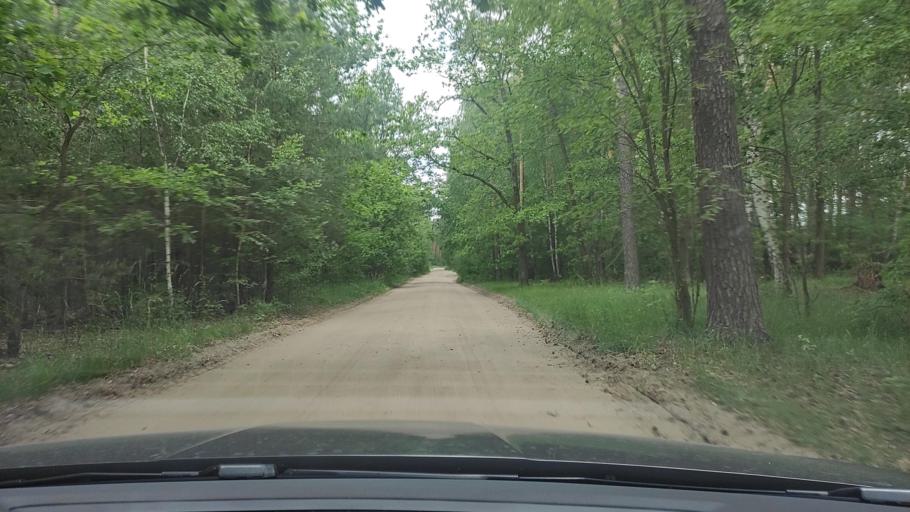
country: PL
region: Greater Poland Voivodeship
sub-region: Powiat poznanski
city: Pobiedziska
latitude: 52.4946
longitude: 17.2003
